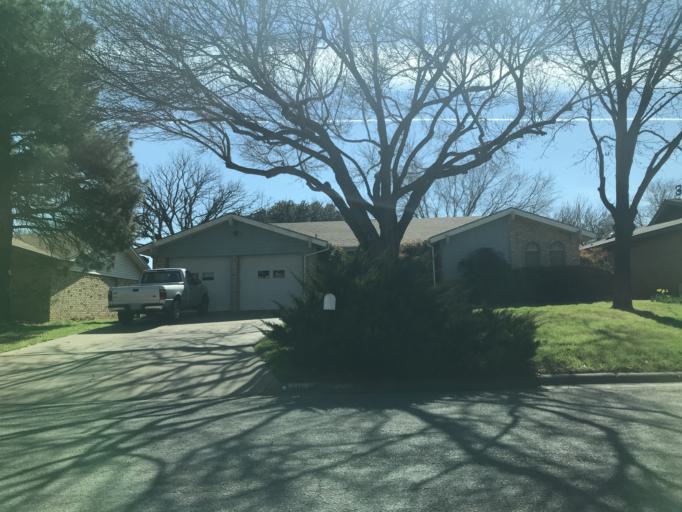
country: US
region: Texas
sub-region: Tom Green County
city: San Angelo
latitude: 31.4352
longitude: -100.4891
